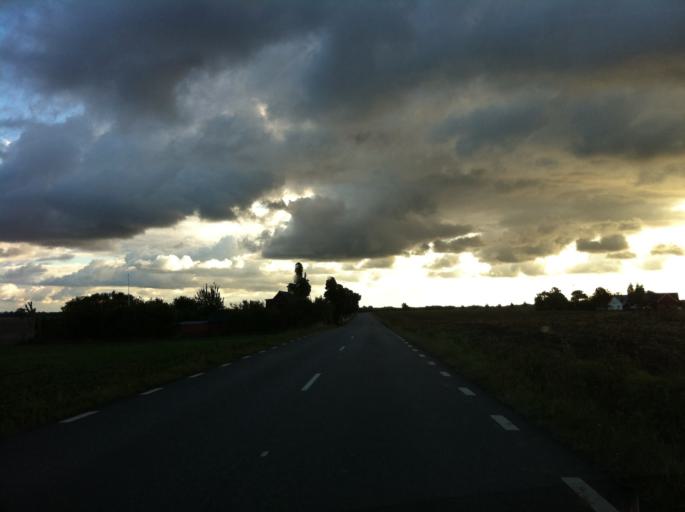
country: SE
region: Skane
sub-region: Svalovs Kommun
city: Svaloev
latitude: 55.8904
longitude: 13.1788
